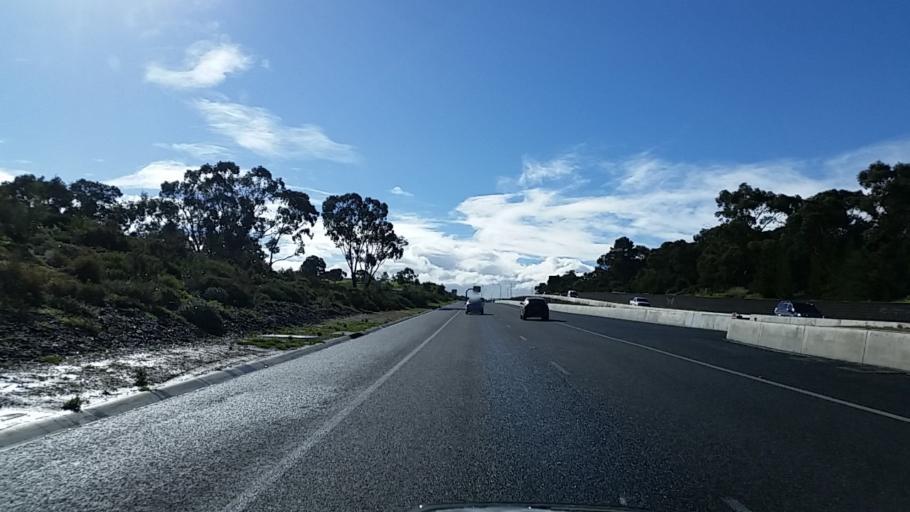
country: AU
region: South Australia
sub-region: Onkaparinga
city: Noarlunga Downs
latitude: -35.1478
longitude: 138.5055
